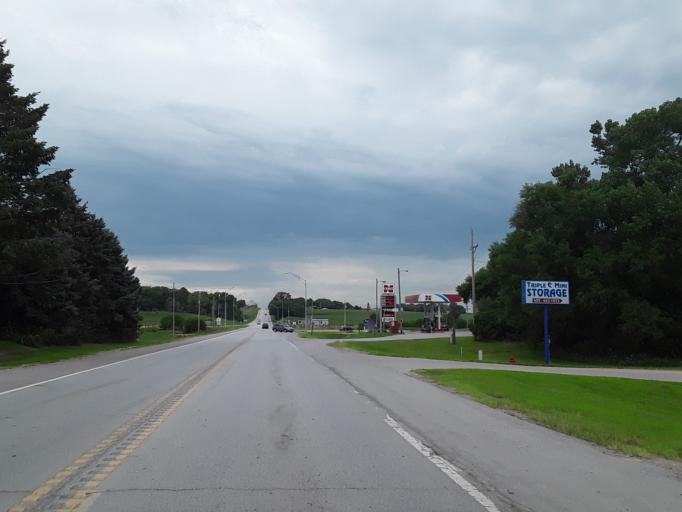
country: US
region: Nebraska
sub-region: Saunders County
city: Yutan
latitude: 41.2338
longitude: -96.3936
